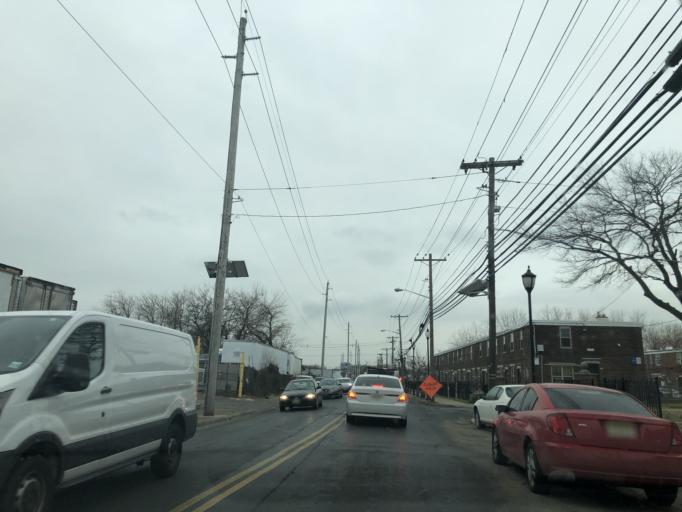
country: US
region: New Jersey
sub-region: Camden County
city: Camden
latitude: 39.9486
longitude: -75.1011
